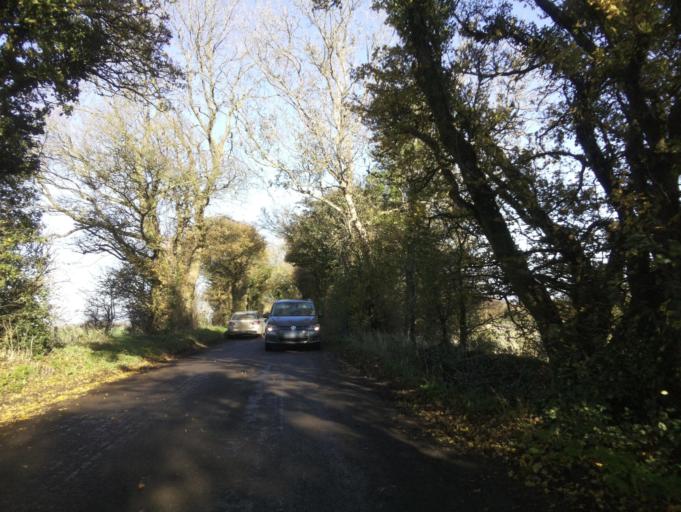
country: GB
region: England
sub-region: Somerset
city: Milborne Port
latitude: 51.0153
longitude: -2.5056
